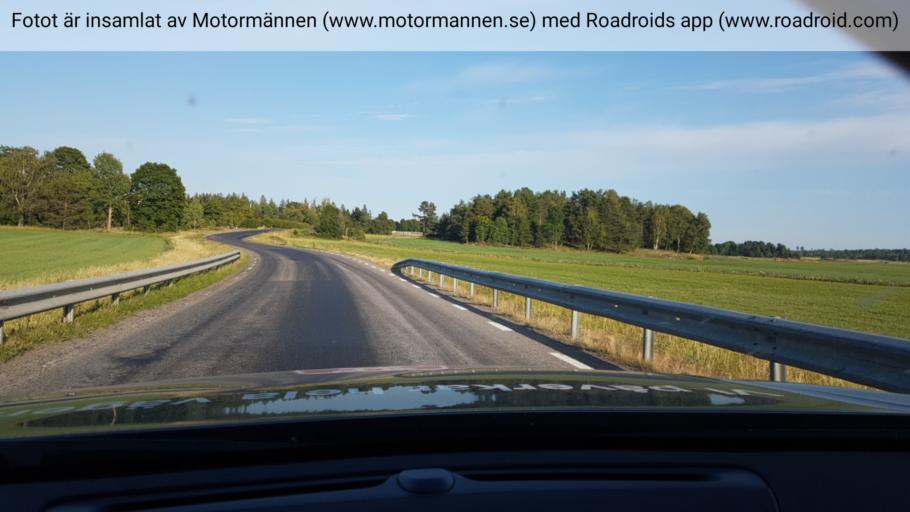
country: SE
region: Uppsala
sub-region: Osthammars Kommun
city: Gimo
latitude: 60.0341
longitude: 18.0388
